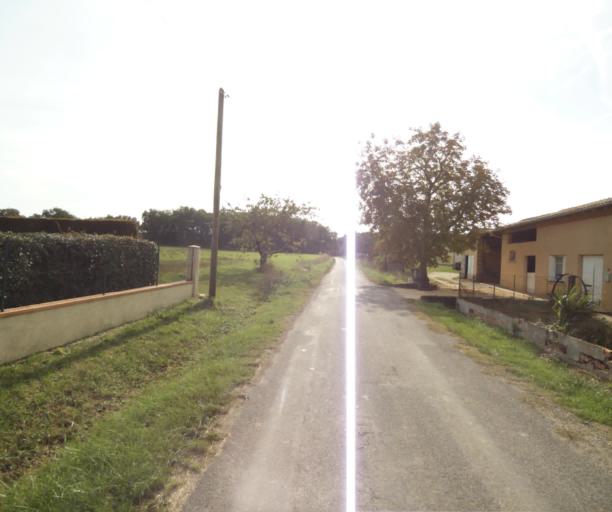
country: FR
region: Midi-Pyrenees
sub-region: Departement du Tarn-et-Garonne
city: Labastide-Saint-Pierre
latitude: 43.9100
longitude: 1.3853
